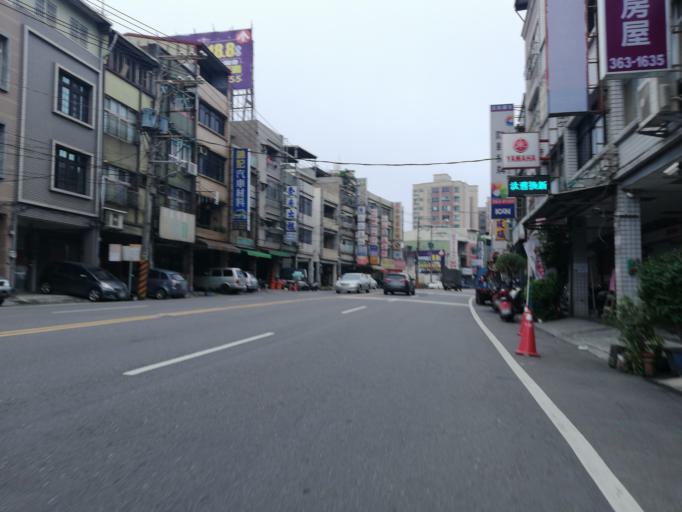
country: TW
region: Taiwan
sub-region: Taoyuan
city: Taoyuan
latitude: 24.9848
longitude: 121.3104
